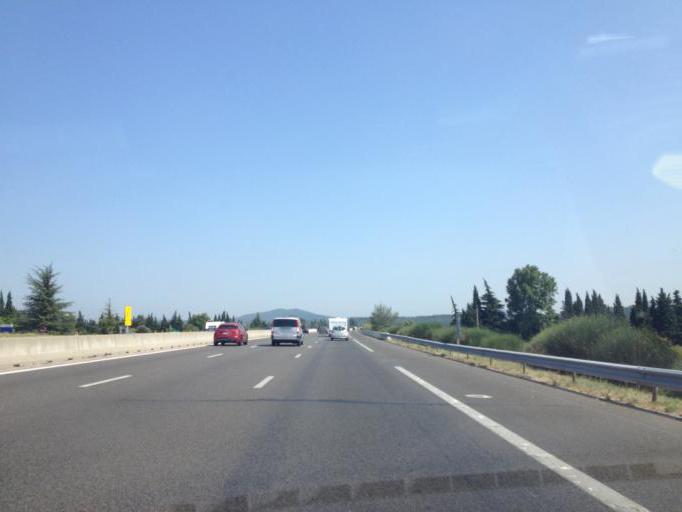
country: FR
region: Rhone-Alpes
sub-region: Departement de la Drome
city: La Garde-Adhemar
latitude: 44.4033
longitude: 4.7292
